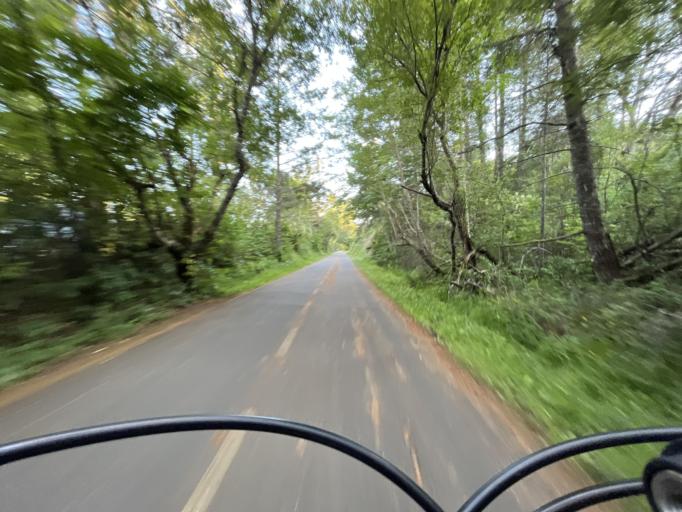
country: CA
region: British Columbia
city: Colwood
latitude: 48.4539
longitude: -123.4698
